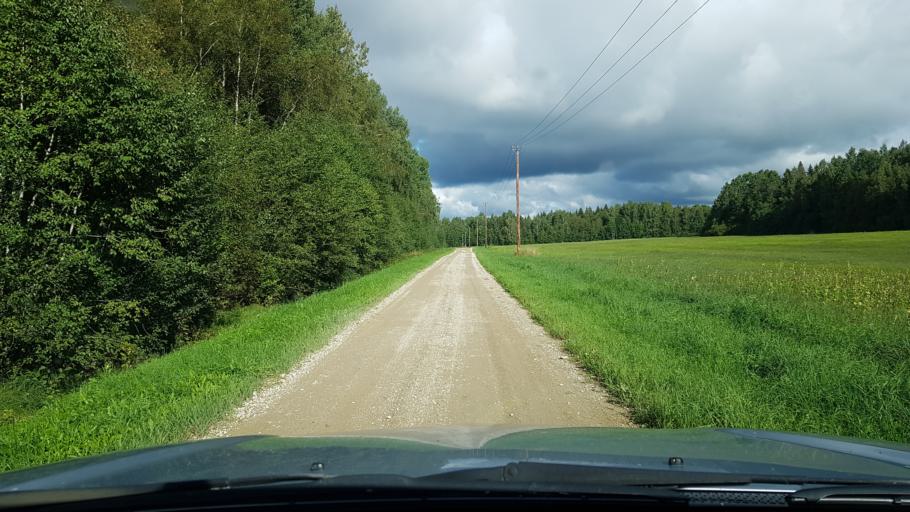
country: EE
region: Harju
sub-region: Rae vald
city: Vaida
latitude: 59.2549
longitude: 25.0558
